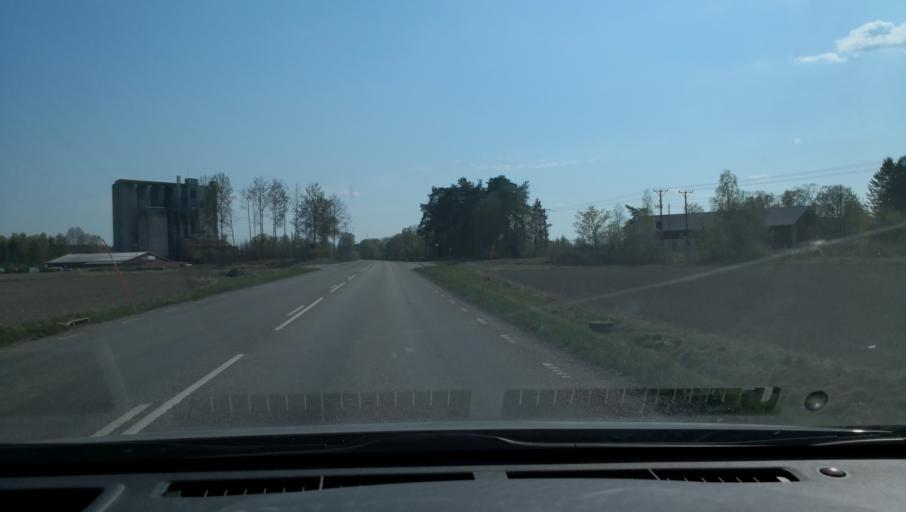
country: SE
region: Vaestmanland
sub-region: Sala Kommun
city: Sala
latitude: 59.9382
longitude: 16.6186
